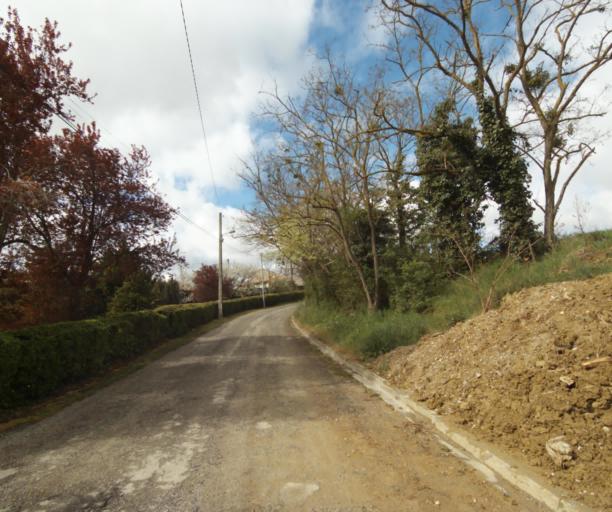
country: FR
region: Midi-Pyrenees
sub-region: Departement de l'Ariege
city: Saverdun
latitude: 43.2322
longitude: 1.5701
